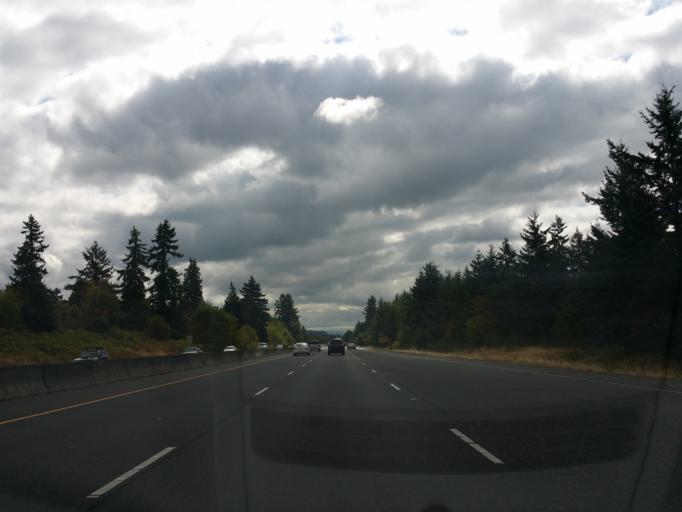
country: US
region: Washington
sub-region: Clark County
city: Mill Plain
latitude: 45.5999
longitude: -122.5352
